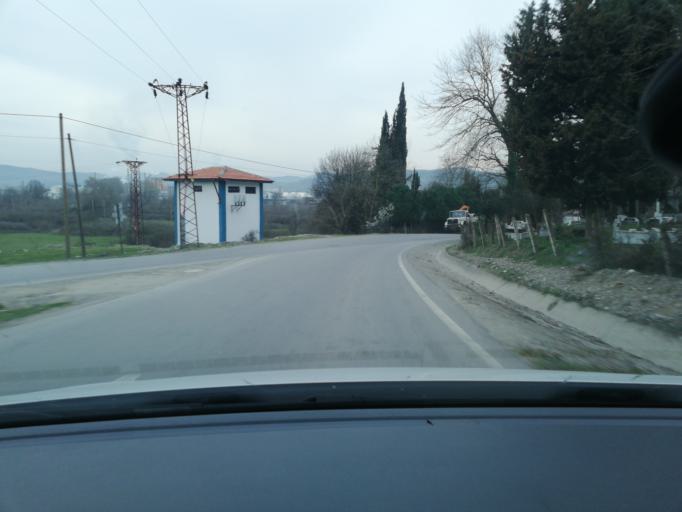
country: TR
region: Zonguldak
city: Caycuma
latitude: 41.4137
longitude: 32.1054
